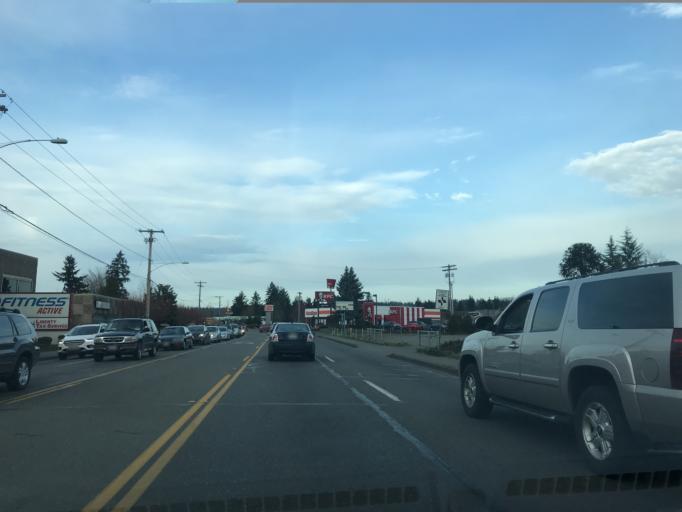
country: US
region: Washington
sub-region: King County
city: Auburn
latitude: 47.3162
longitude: -122.2228
